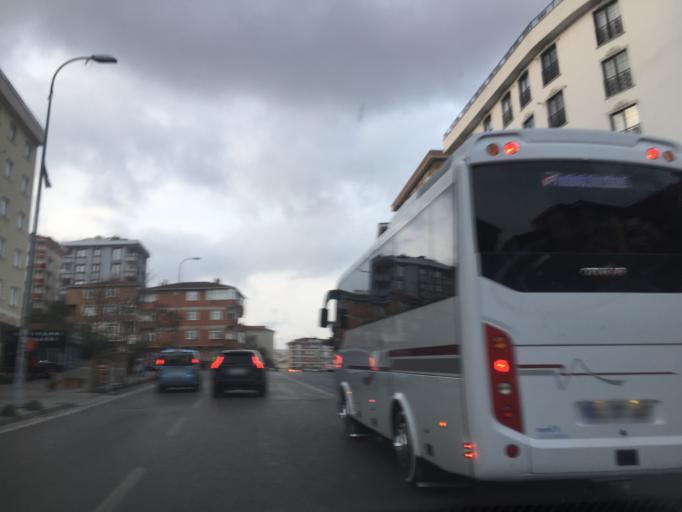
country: TR
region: Istanbul
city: Samandira
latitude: 40.9876
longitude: 29.2321
